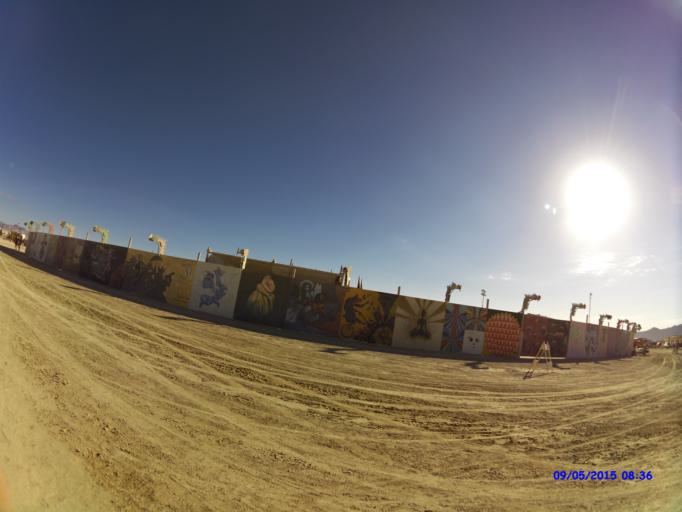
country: US
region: Nevada
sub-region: Pershing County
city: Lovelock
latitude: 40.7803
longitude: -119.2147
